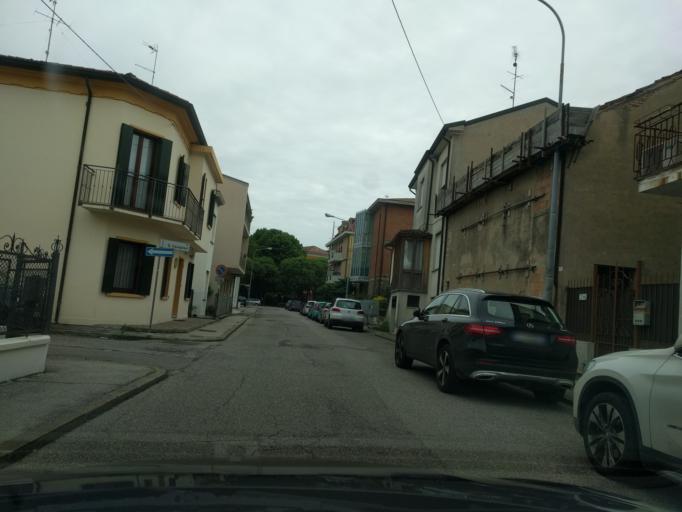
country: IT
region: Veneto
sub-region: Provincia di Rovigo
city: Rovigo
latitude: 45.0689
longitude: 11.7855
